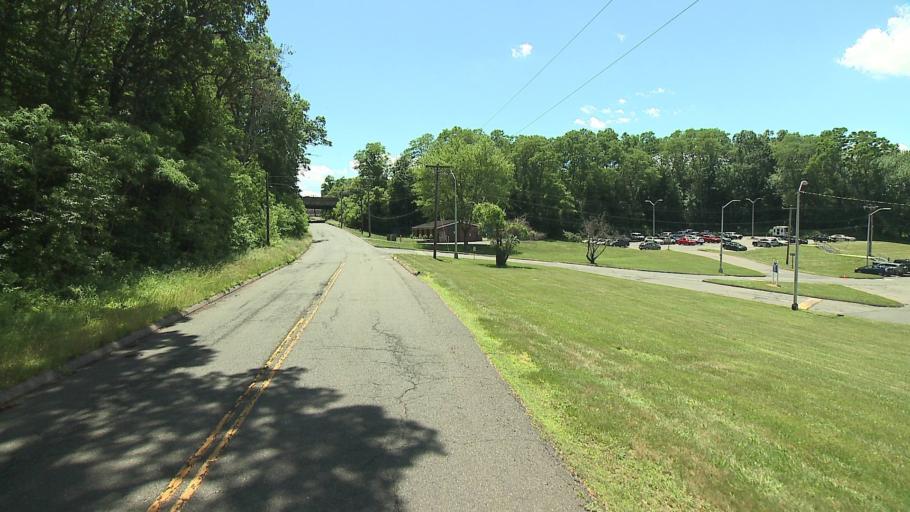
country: US
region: Connecticut
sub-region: Hartford County
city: Newington
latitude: 41.7012
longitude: -72.7147
